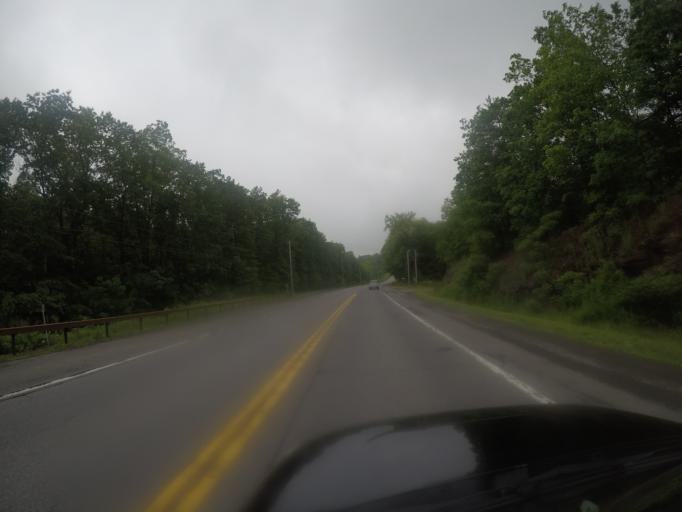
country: US
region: New York
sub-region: Ulster County
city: West Hurley
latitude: 41.9931
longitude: -74.1594
